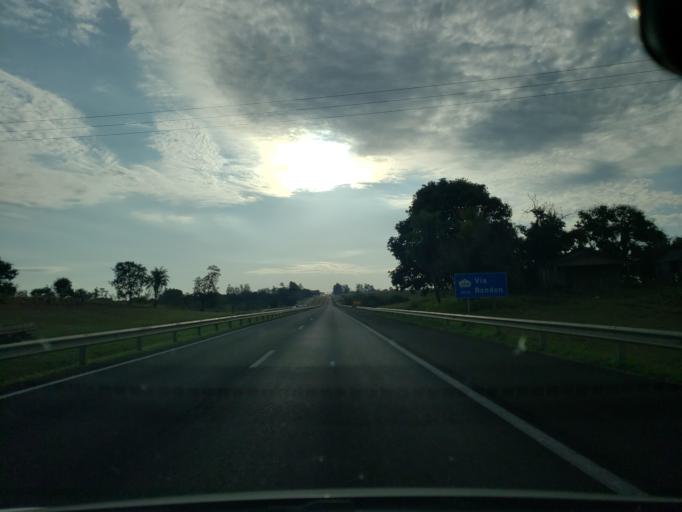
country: BR
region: Sao Paulo
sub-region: Mirandopolis
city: Mirandopolis
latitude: -21.0811
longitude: -51.0710
